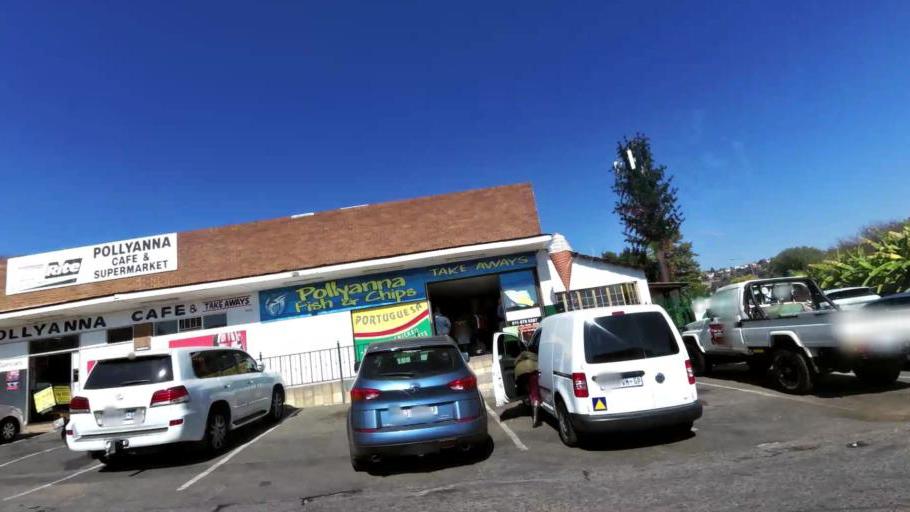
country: ZA
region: Gauteng
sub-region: City of Johannesburg Metropolitan Municipality
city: Roodepoort
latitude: -26.1445
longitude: 27.9368
